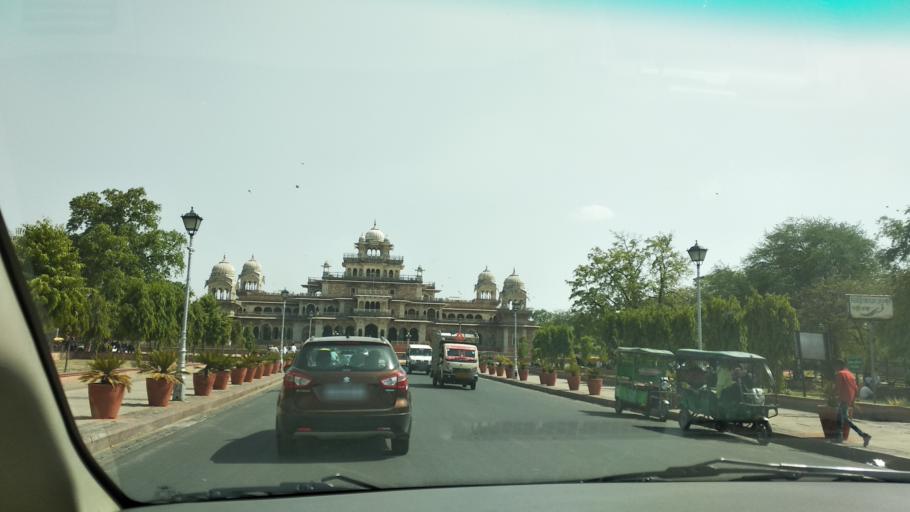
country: IN
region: Rajasthan
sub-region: Jaipur
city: Jaipur
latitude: 26.9131
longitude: 75.8199
